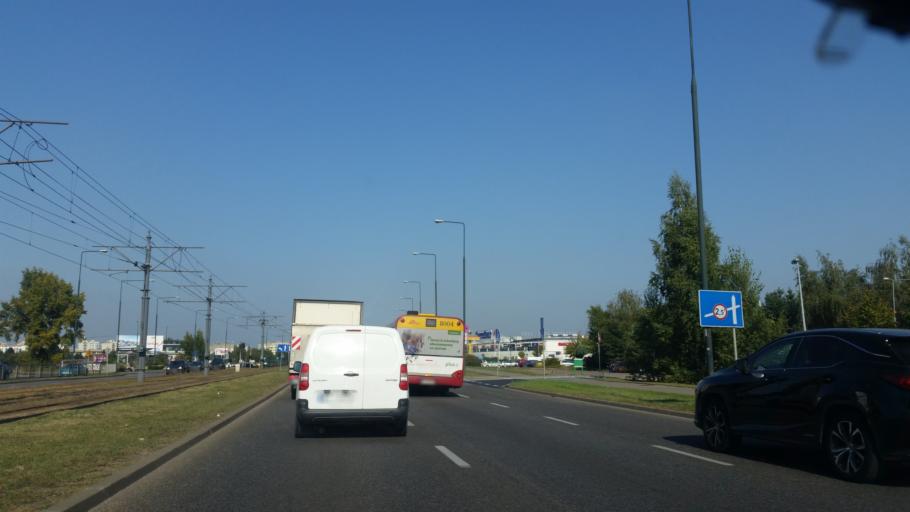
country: PL
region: Masovian Voivodeship
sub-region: Warszawa
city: Bemowo
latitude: 52.2621
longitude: 20.9259
